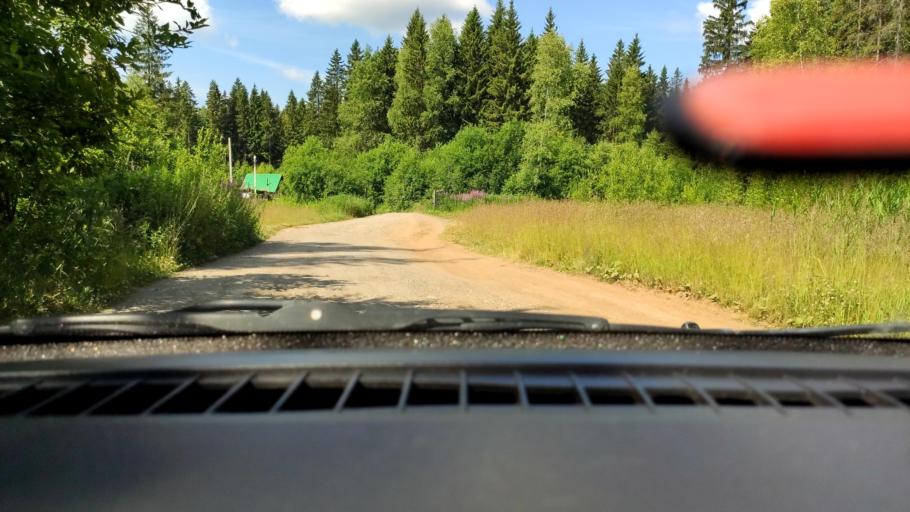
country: RU
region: Perm
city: Perm
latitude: 58.1464
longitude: 56.2909
